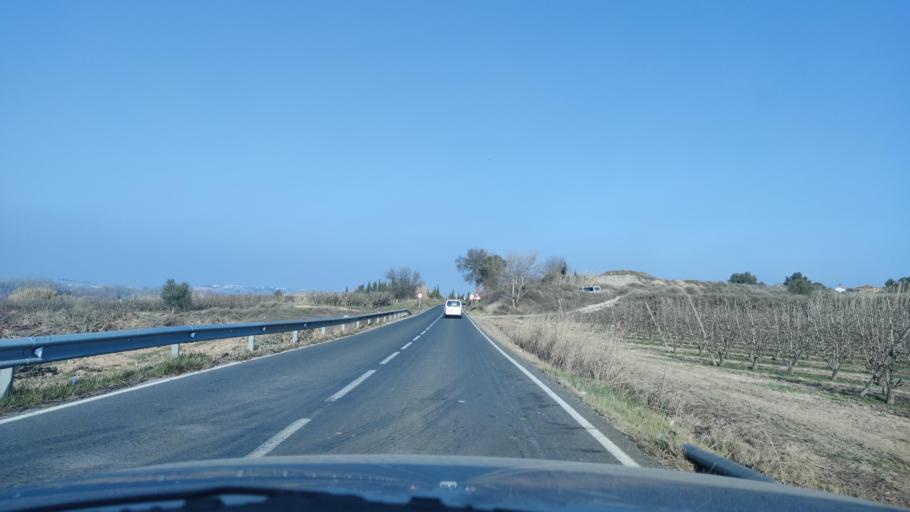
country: ES
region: Catalonia
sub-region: Provincia de Lleida
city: Sunyer
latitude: 41.5665
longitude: 0.5907
